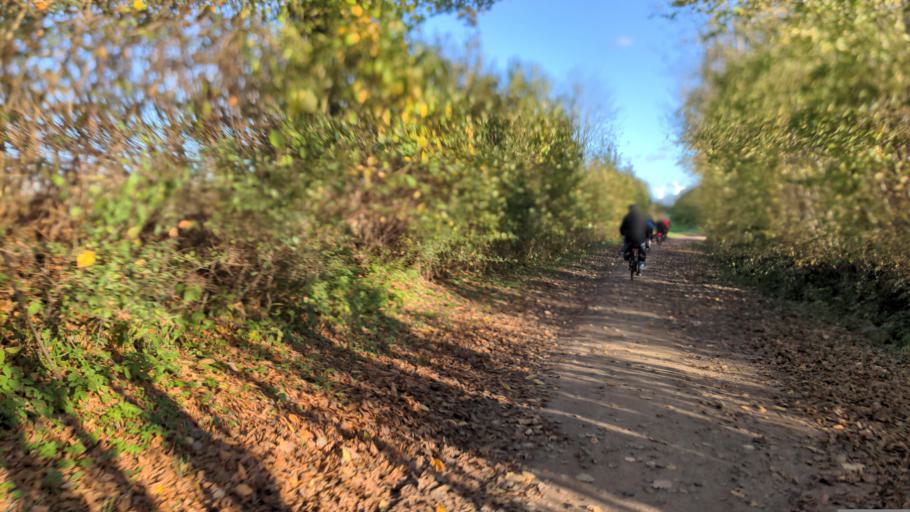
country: DE
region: Schleswig-Holstein
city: Ratekau
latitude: 53.9403
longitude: 10.7646
